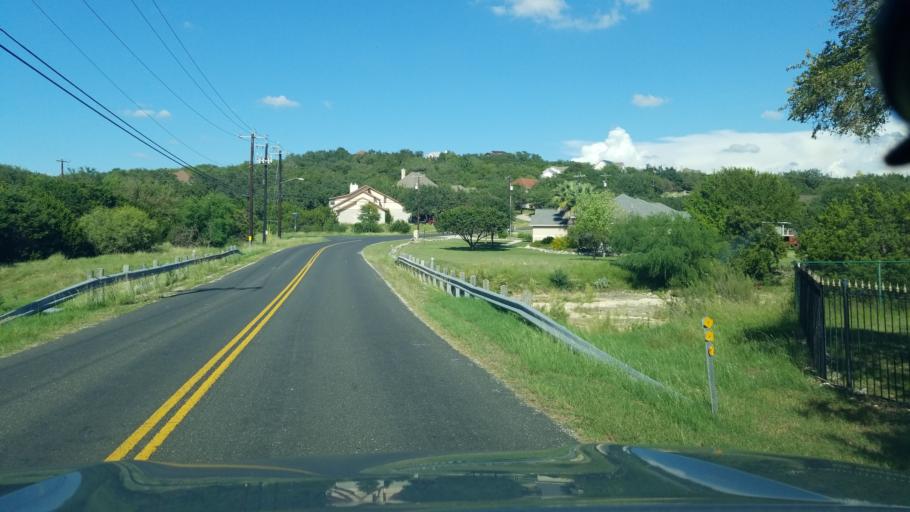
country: US
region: Texas
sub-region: Bexar County
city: Timberwood Park
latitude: 29.6831
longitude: -98.4955
